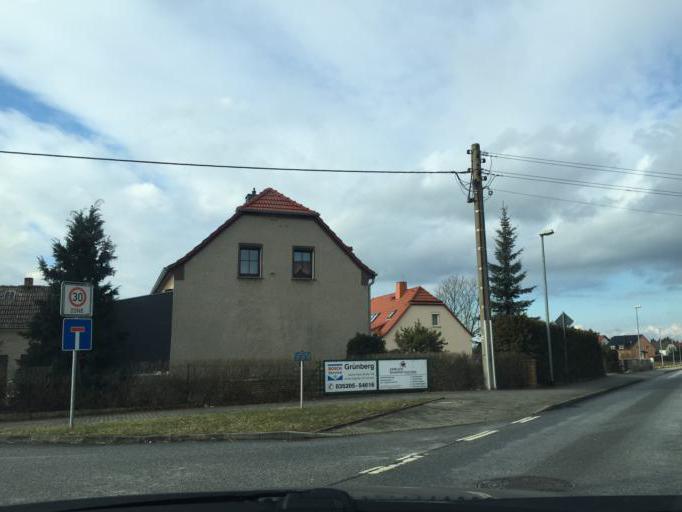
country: DE
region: Saxony
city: Ottendorf-Okrilla
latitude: 51.1793
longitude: 13.8498
